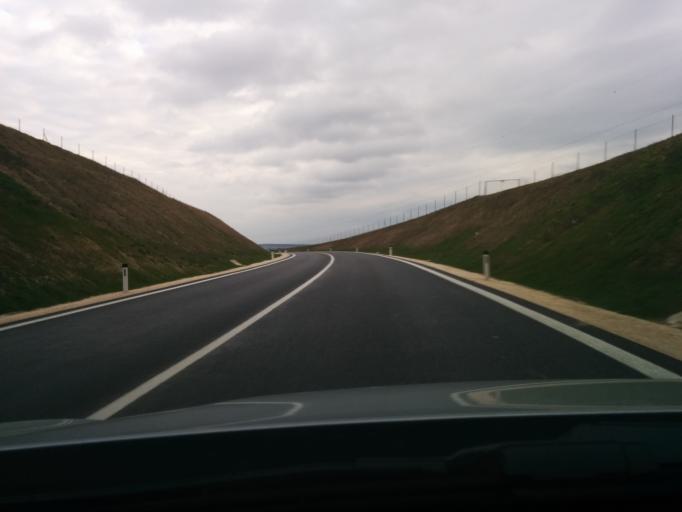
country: AT
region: Lower Austria
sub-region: Politischer Bezirk Mistelbach
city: Mistelbach
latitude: 48.5825
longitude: 16.5539
